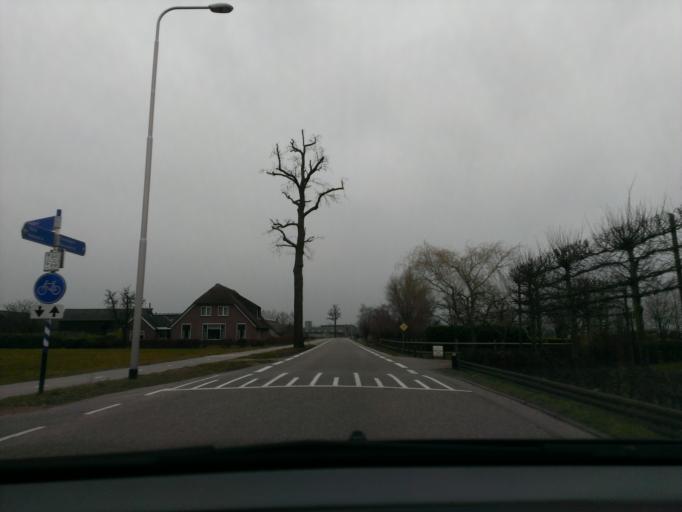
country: NL
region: Gelderland
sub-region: Gemeente Epe
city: Emst
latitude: 52.2927
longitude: 6.0152
